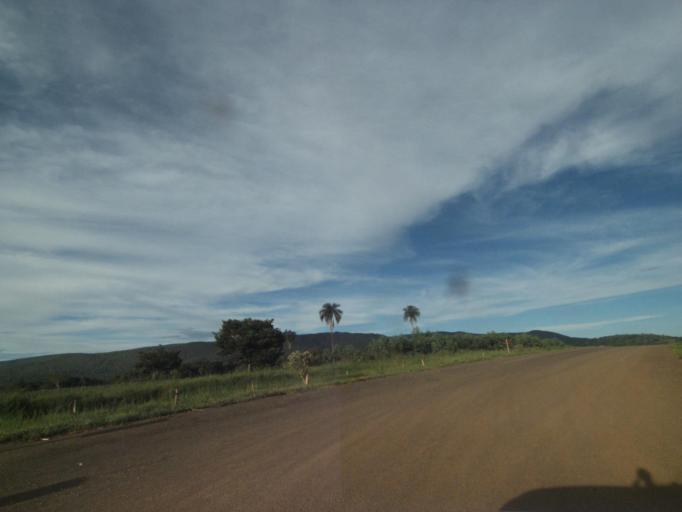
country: BR
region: Goias
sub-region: Jaragua
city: Jaragua
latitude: -15.8422
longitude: -49.3571
